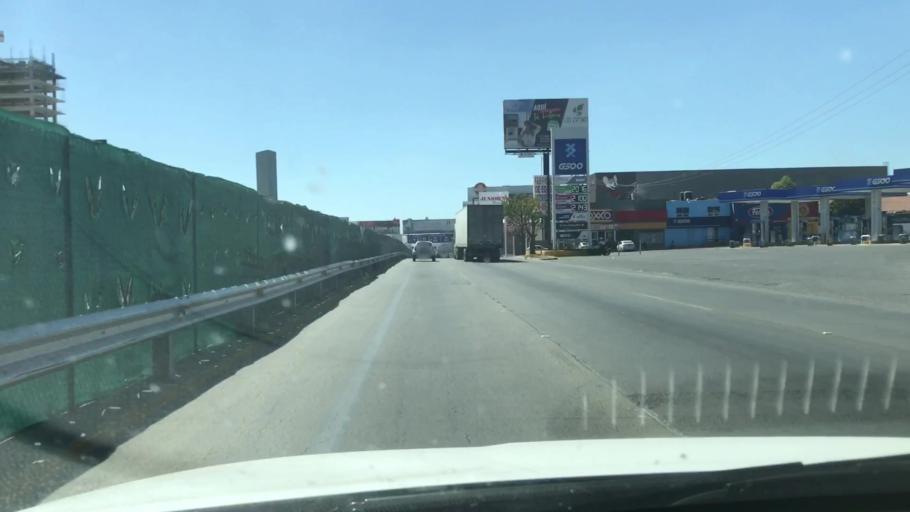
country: MX
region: Jalisco
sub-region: Tlajomulco de Zuniga
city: La Tijera
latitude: 20.5726
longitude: -103.4553
